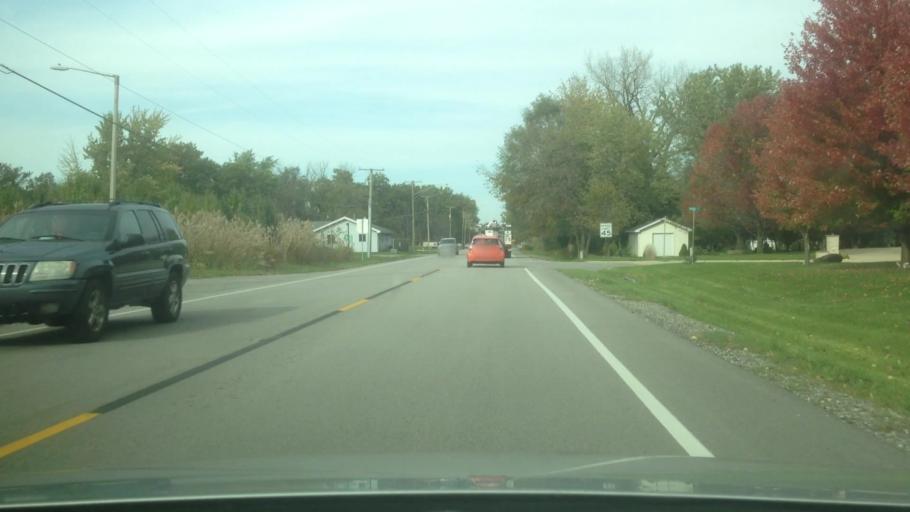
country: US
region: Illinois
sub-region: Will County
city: Wilmington
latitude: 41.2991
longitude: -88.1587
